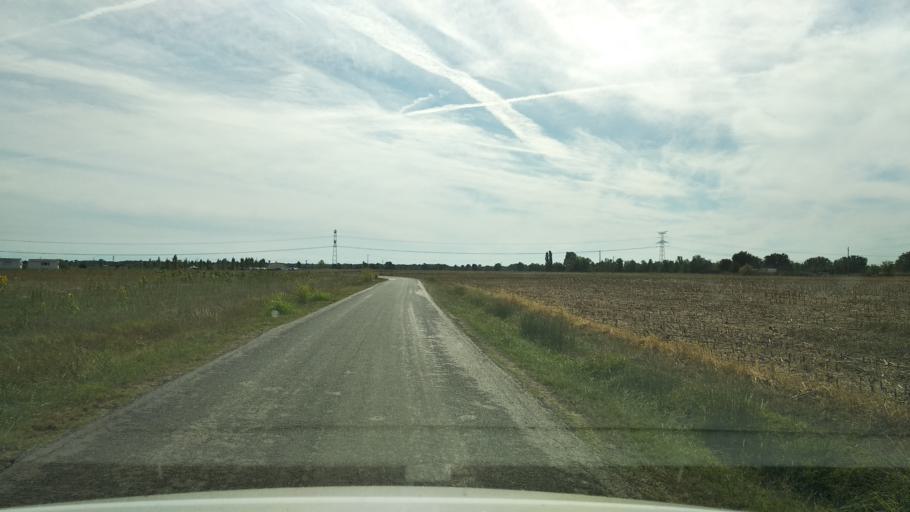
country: FR
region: Midi-Pyrenees
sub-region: Departement du Tarn-et-Garonne
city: Pompignan
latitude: 43.8082
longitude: 1.3115
